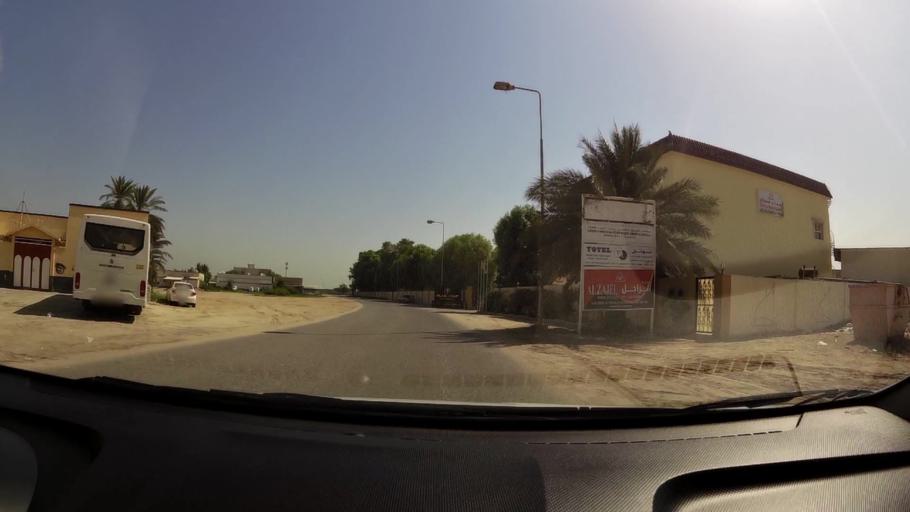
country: AE
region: Umm al Qaywayn
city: Umm al Qaywayn
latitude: 25.5829
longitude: 55.5778
